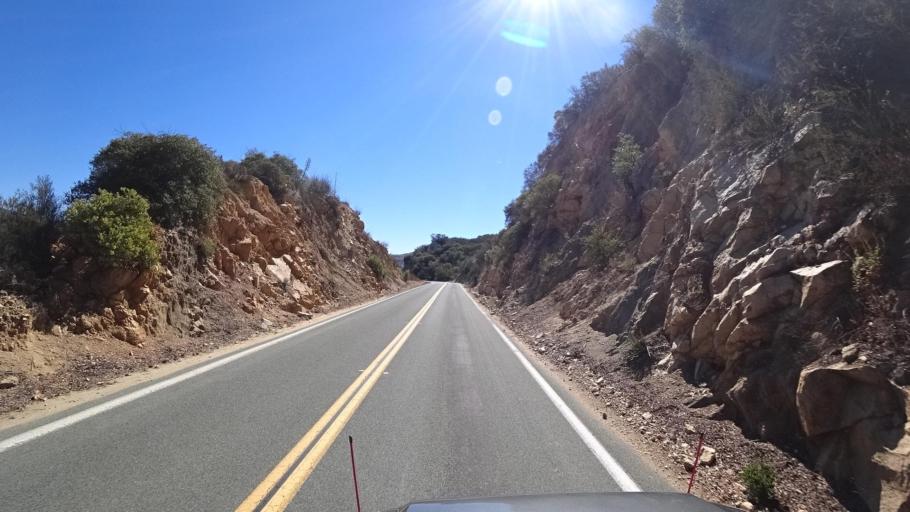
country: US
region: California
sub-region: San Diego County
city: Descanso
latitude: 32.7504
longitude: -116.6690
